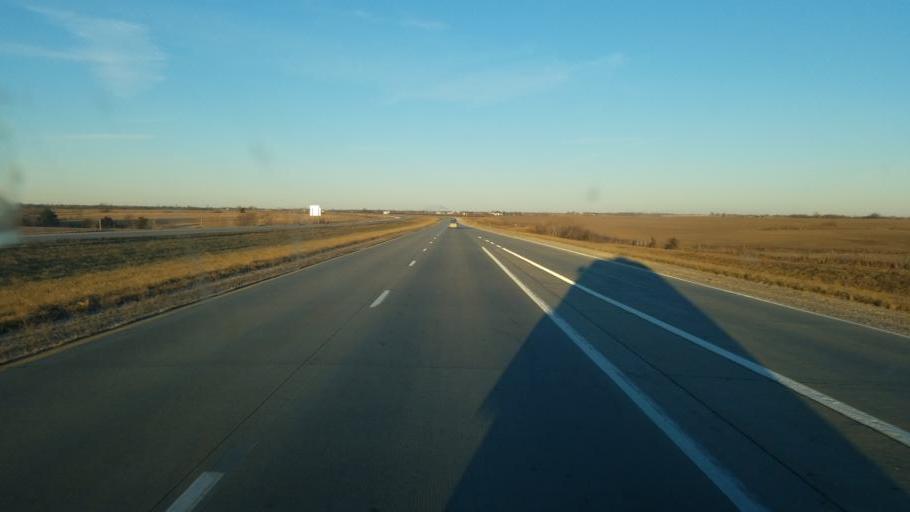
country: US
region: Iowa
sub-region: Wapello County
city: Ottumwa
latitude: 41.0001
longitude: -92.2423
